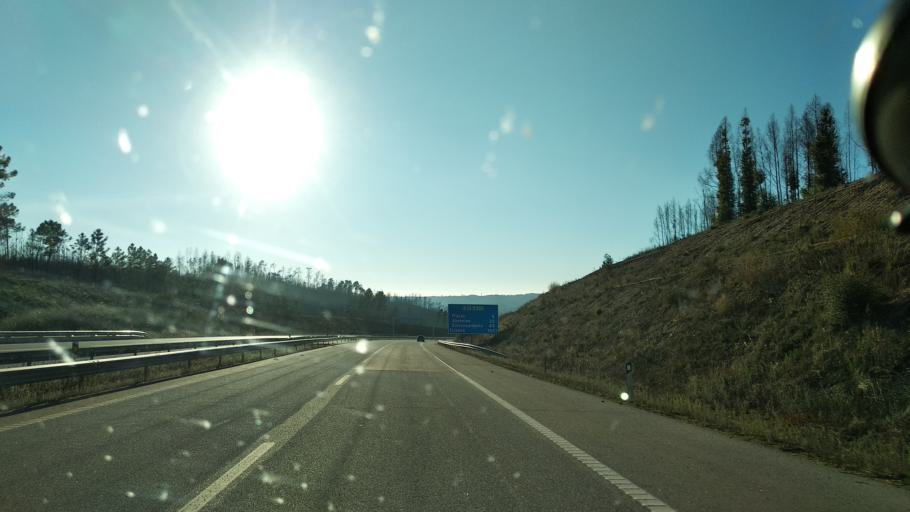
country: PT
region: Santarem
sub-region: Macao
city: Macao
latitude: 39.5273
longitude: -7.9591
